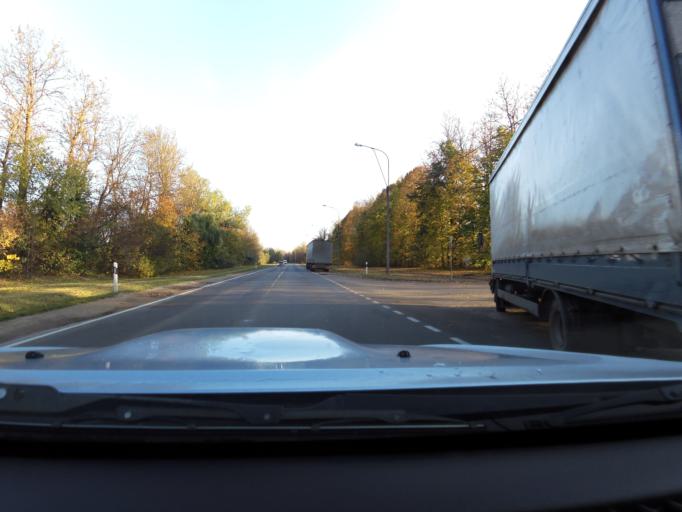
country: LT
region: Vilnius County
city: Vilkpede
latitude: 54.6394
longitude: 25.2593
